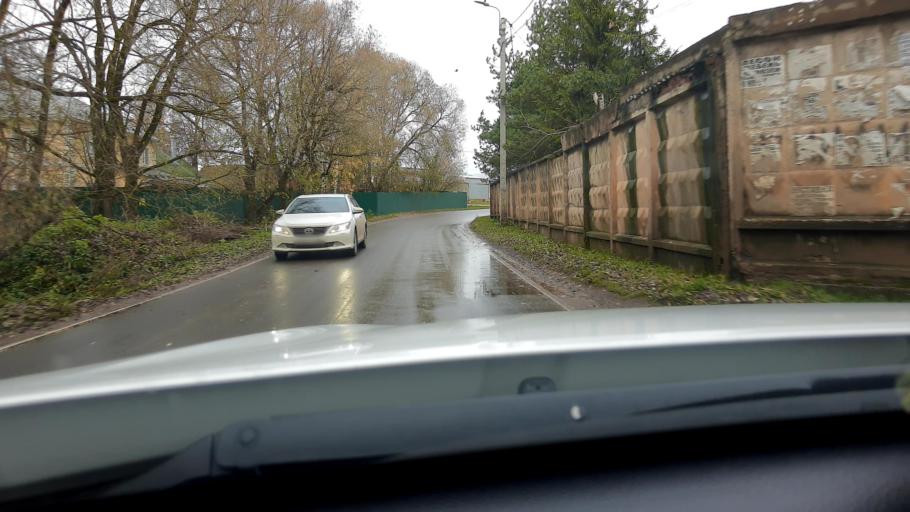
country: RU
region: Moskovskaya
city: Annino
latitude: 55.5662
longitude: 37.2357
